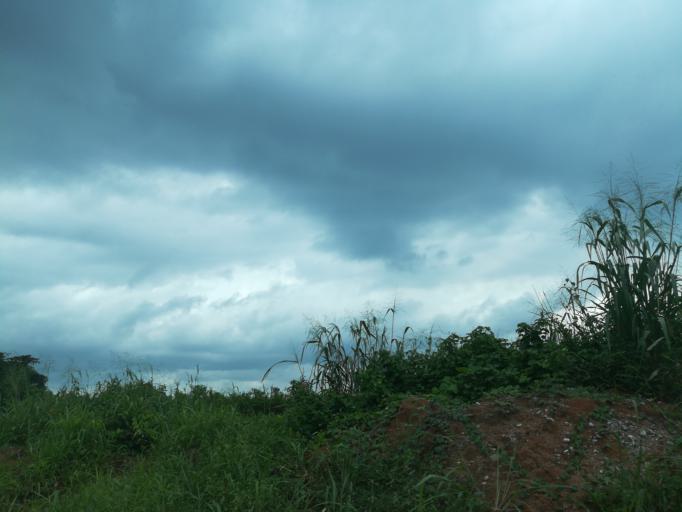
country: NG
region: Lagos
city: Ejirin
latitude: 6.6460
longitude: 3.8426
